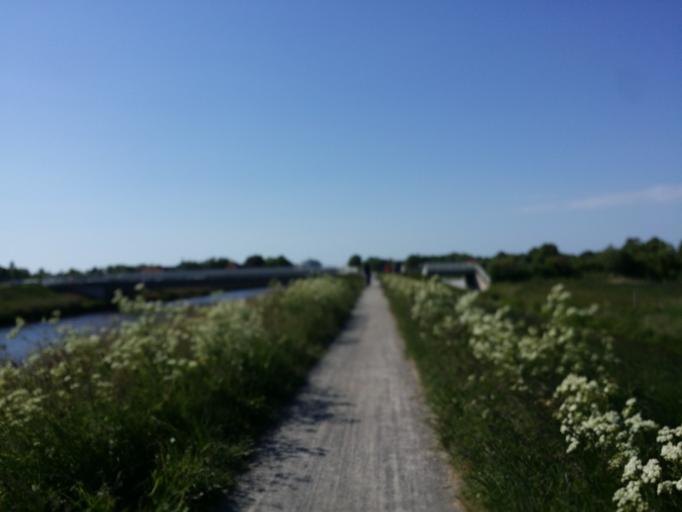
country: DE
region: Lower Saxony
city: Moorweg
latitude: 53.6692
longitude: 7.5823
